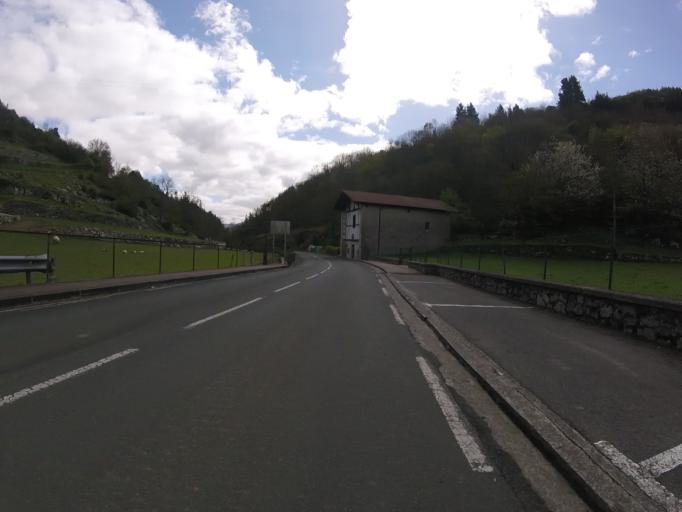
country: ES
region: Basque Country
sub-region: Provincia de Guipuzcoa
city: Albiztur
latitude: 43.1288
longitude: -2.1284
